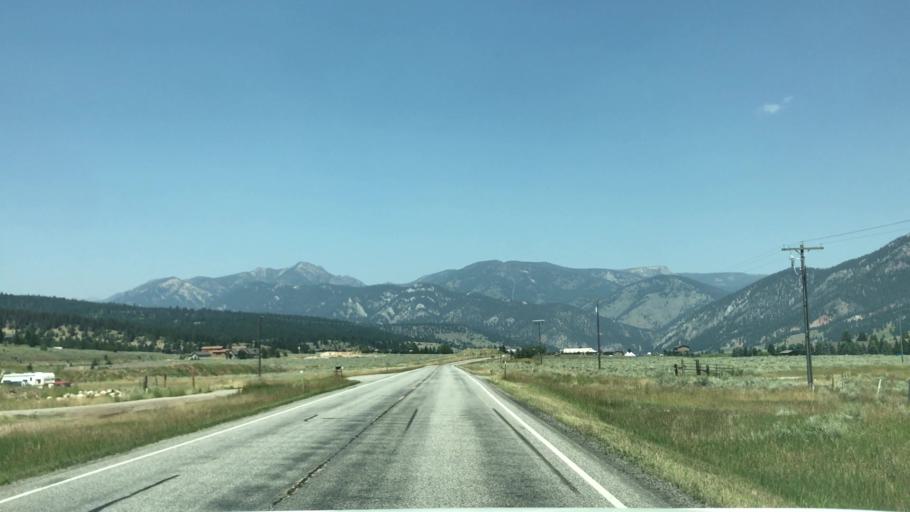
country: US
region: Montana
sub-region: Gallatin County
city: Big Sky
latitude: 45.2167
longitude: -111.2492
